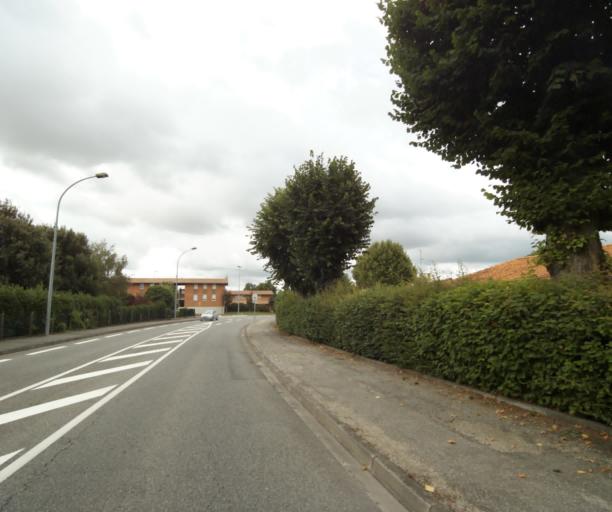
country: FR
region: Midi-Pyrenees
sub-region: Departement de la Haute-Garonne
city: Balma
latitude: 43.5945
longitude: 1.5067
